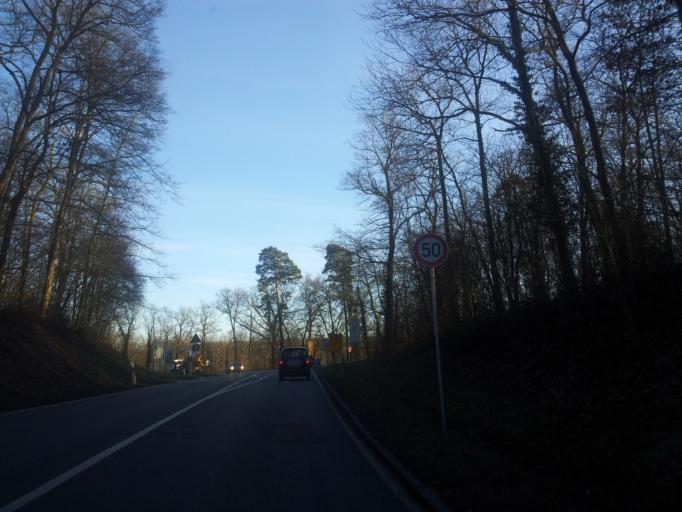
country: DE
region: Baden-Wuerttemberg
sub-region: Regierungsbezirk Stuttgart
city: Flein
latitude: 49.0857
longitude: 9.2253
